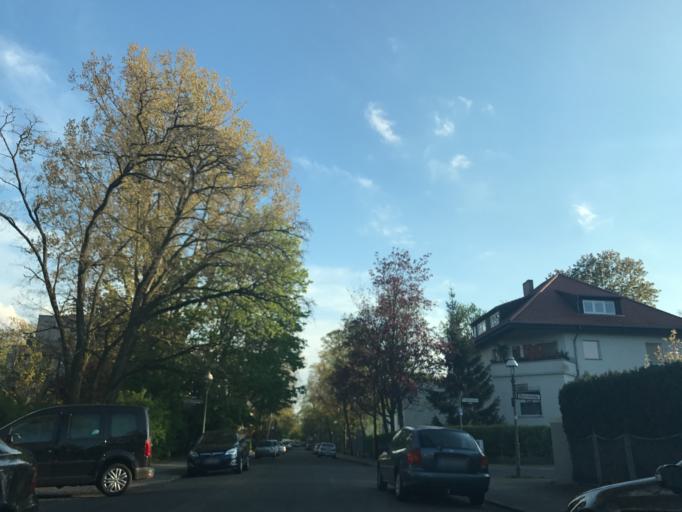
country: DE
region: Berlin
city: Westend
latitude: 52.5146
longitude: 13.2762
